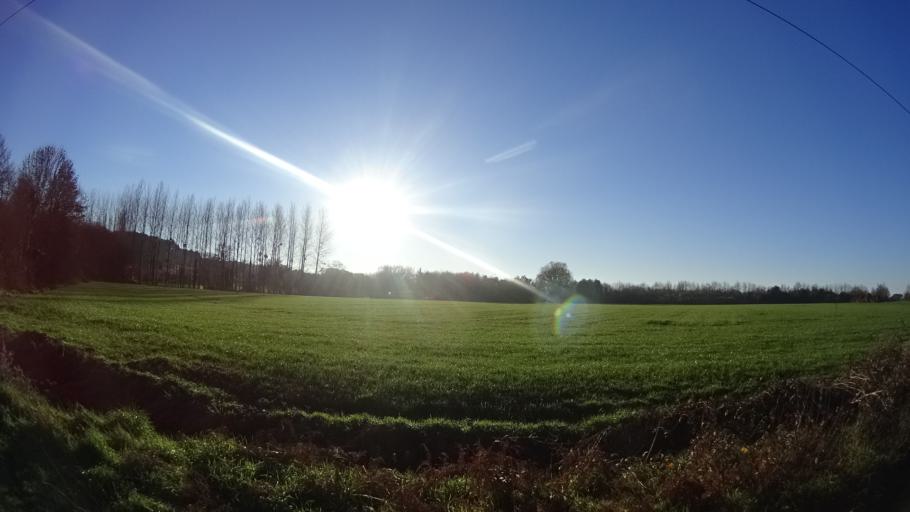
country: FR
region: Brittany
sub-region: Departement du Morbihan
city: Allaire
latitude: 47.6532
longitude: -2.1613
